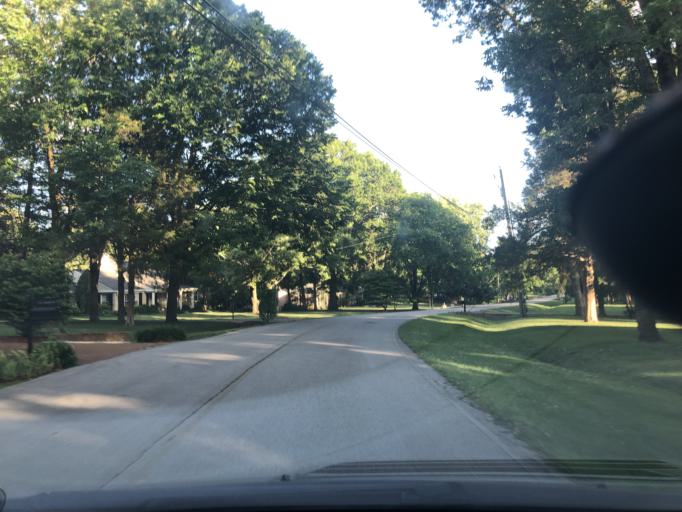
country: US
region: Tennessee
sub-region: Davidson County
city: Forest Hills
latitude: 36.0627
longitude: -86.8446
